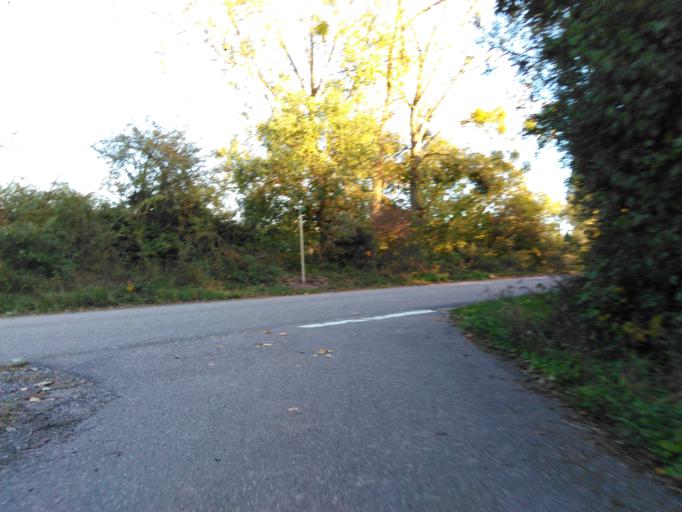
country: FR
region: Lorraine
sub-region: Departement de la Moselle
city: Argancy
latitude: 49.1996
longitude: 6.1847
